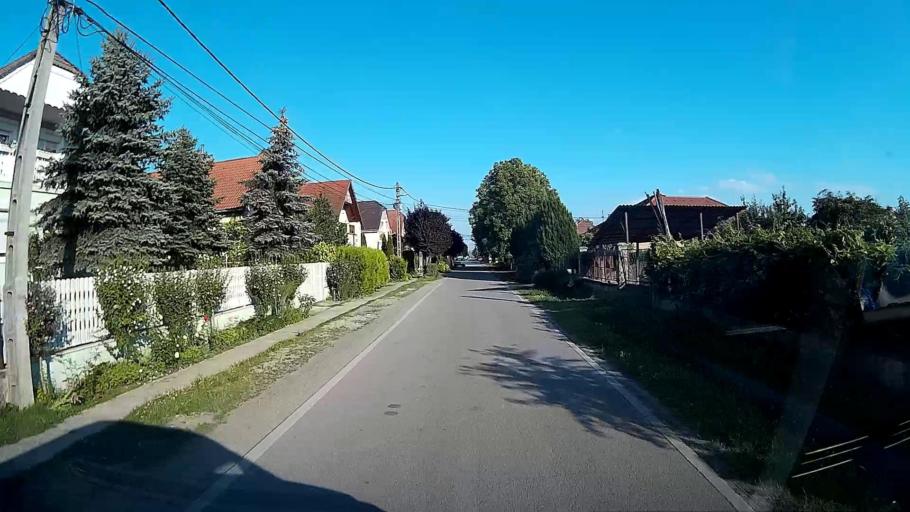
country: HU
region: Pest
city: Tahitotfalu
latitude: 47.7540
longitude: 19.0972
